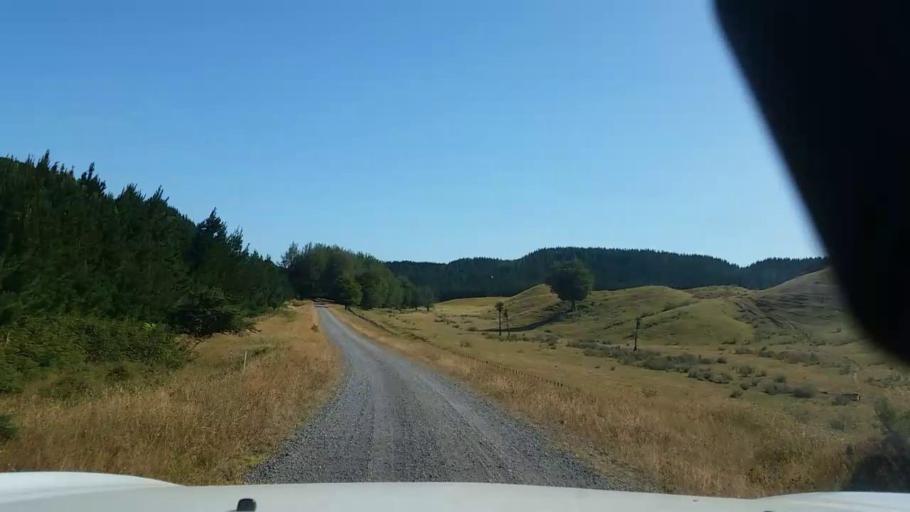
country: NZ
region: Bay of Plenty
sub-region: Western Bay of Plenty District
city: Maketu
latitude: -37.9737
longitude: 176.4087
